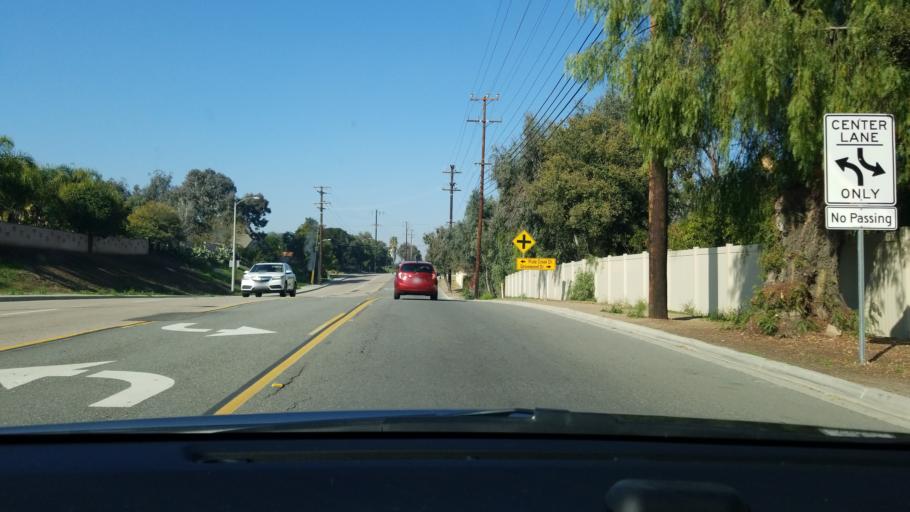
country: US
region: California
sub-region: Riverside County
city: El Cerrito
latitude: 33.8400
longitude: -117.5296
